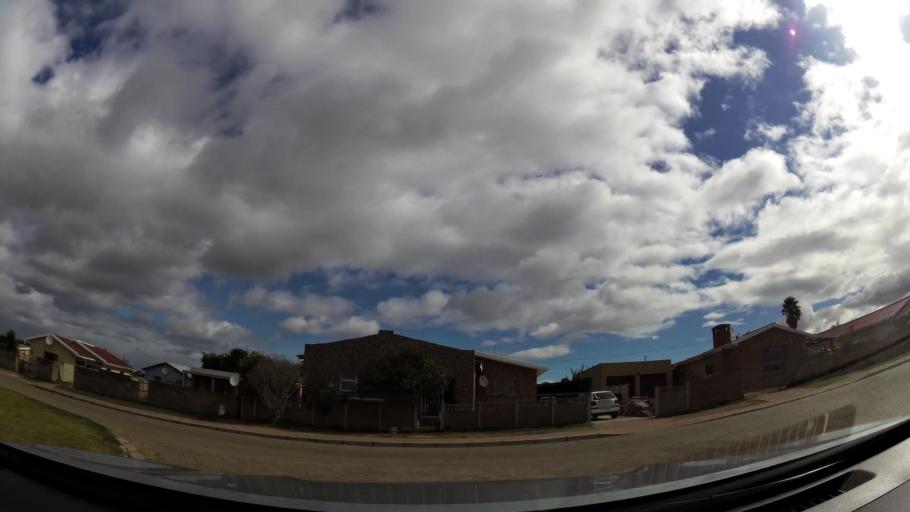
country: ZA
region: Western Cape
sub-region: Eden District Municipality
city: George
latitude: -34.0224
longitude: 22.4704
